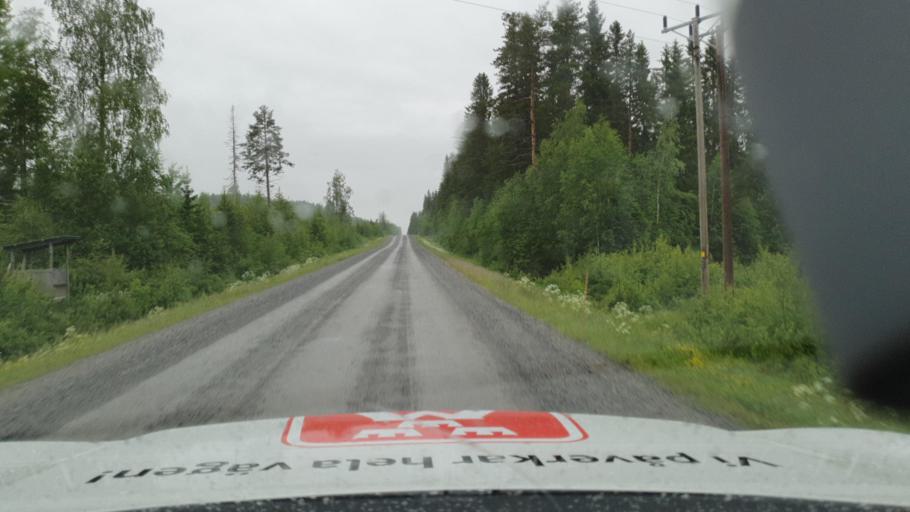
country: SE
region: Vaesterbotten
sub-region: Bjurholms Kommun
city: Bjurholm
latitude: 63.8493
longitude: 19.4763
